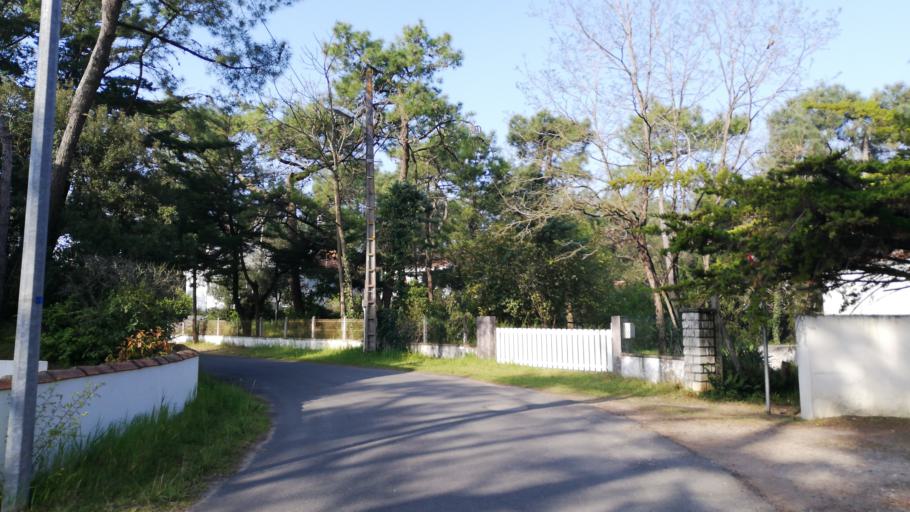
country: FR
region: Pays de la Loire
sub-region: Departement de la Vendee
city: La Tranche-sur-Mer
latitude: 46.3475
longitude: -1.4147
